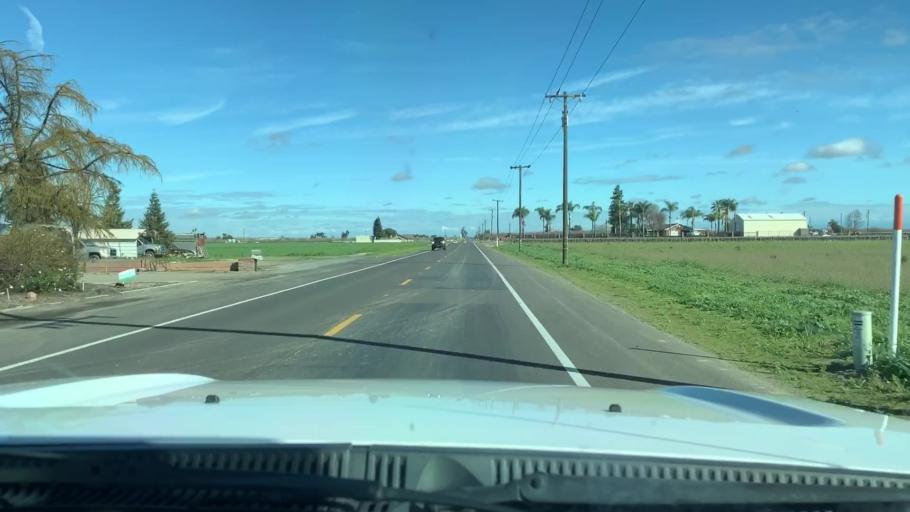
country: US
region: California
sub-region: Fresno County
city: Laton
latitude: 36.4926
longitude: -119.6830
